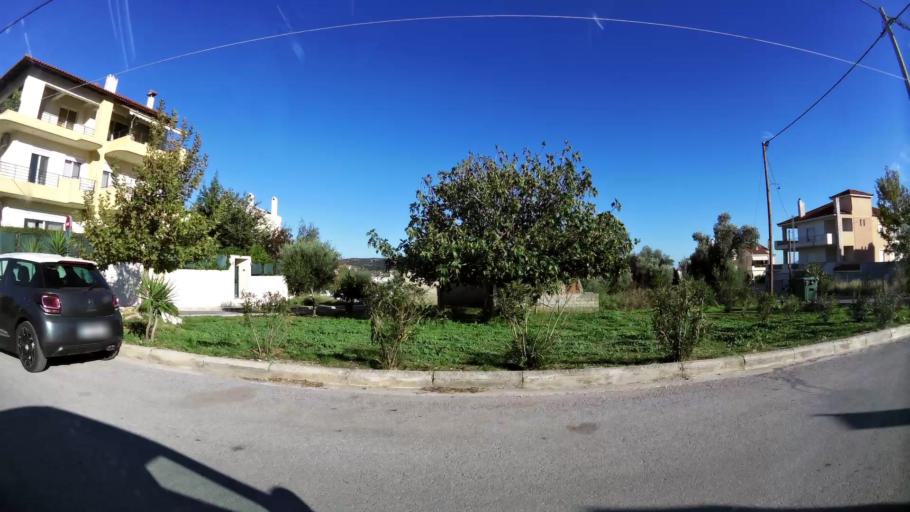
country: GR
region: Attica
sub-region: Nomarchia Anatolikis Attikis
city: Paiania
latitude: 37.9647
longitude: 23.8484
